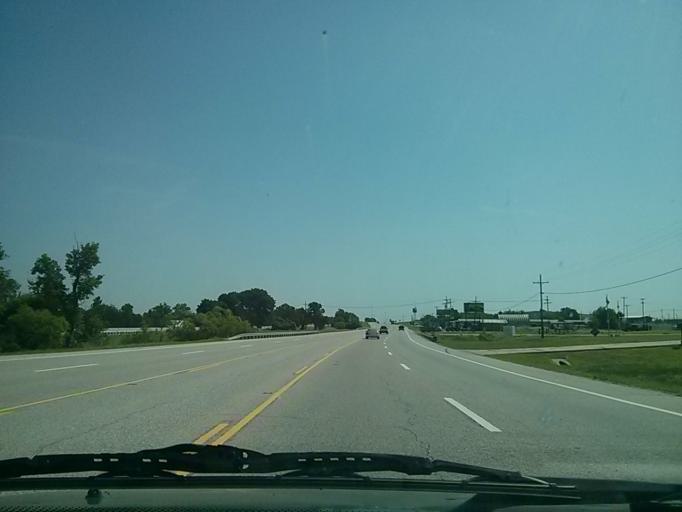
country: US
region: Oklahoma
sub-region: Tulsa County
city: Oakhurst
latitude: 36.0672
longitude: -96.0654
